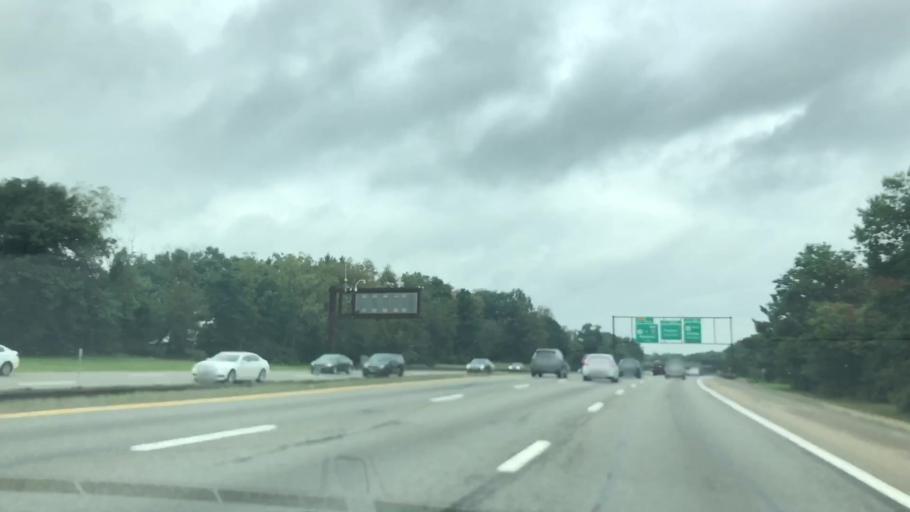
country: US
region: New Jersey
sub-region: Passaic County
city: Clifton
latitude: 40.8640
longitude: -74.1718
